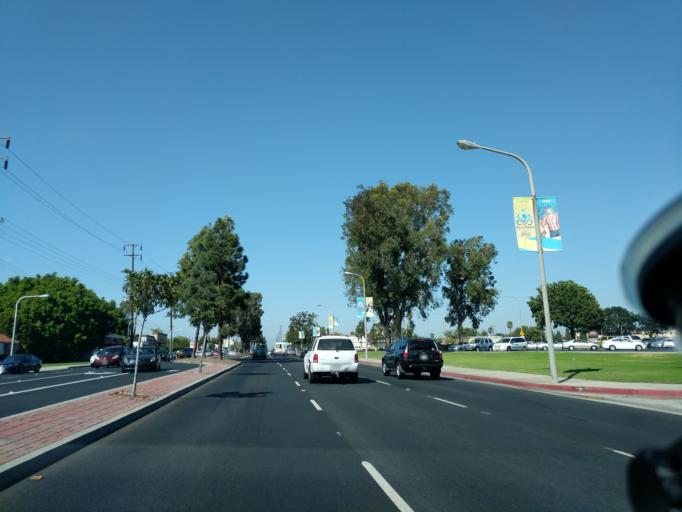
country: US
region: California
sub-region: Orange County
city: Cypress
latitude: 33.8288
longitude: -118.0283
